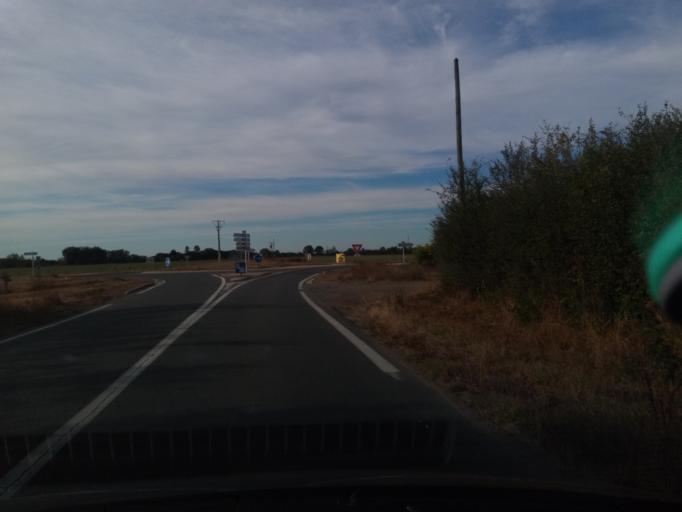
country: FR
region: Poitou-Charentes
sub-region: Departement de la Vienne
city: Saulge
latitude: 46.4049
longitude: 0.8922
